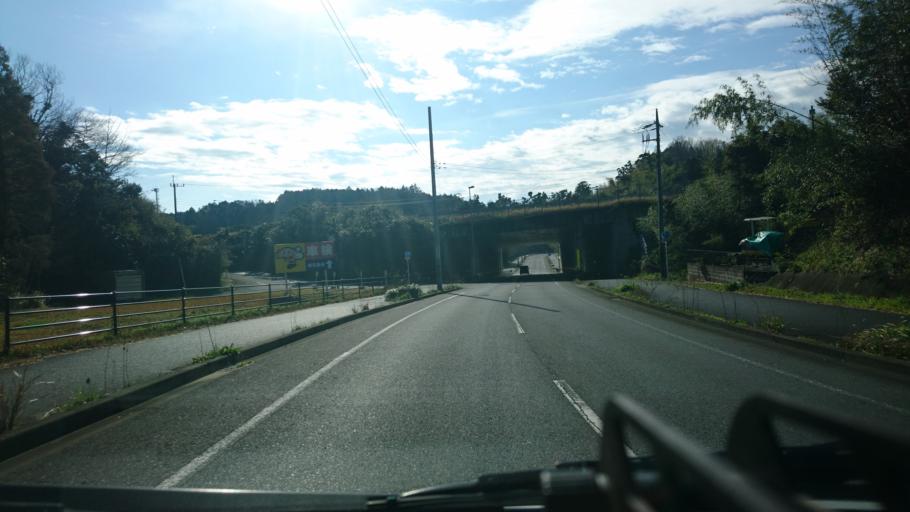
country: JP
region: Chiba
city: Kisarazu
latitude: 35.3537
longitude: 139.9413
